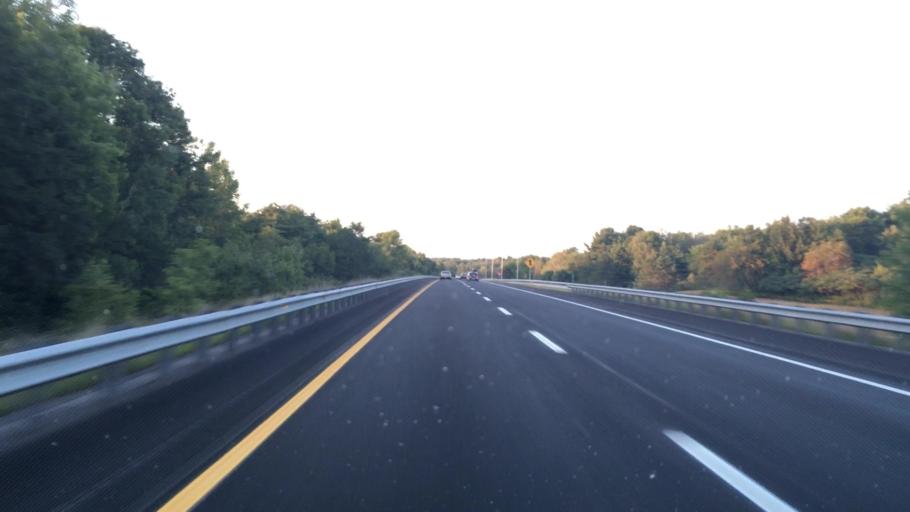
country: US
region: Maine
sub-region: Sagadahoc County
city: Topsham
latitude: 44.0183
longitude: -69.9192
